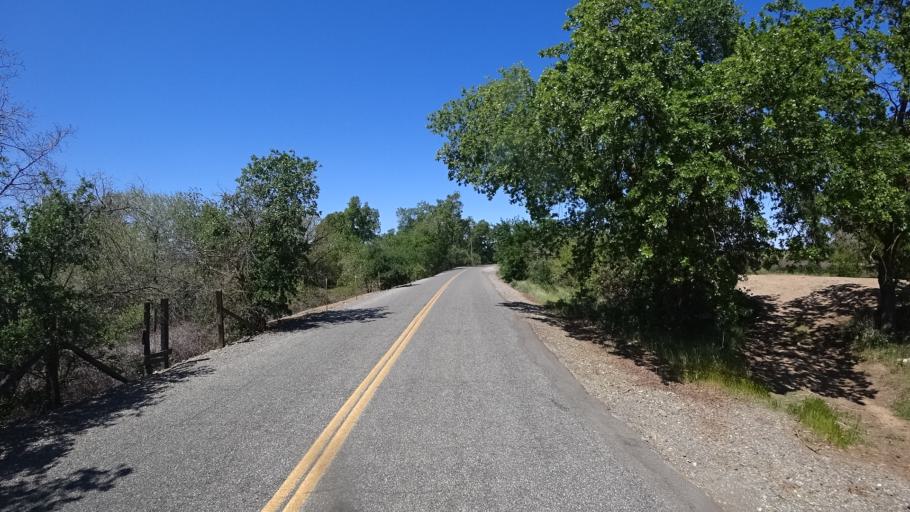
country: US
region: California
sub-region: Glenn County
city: Orland
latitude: 39.7899
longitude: -122.2253
